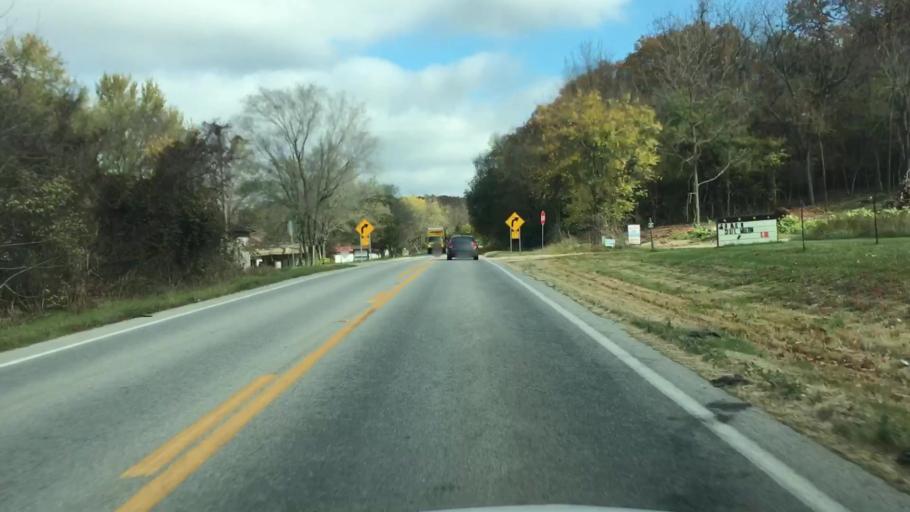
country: US
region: Arkansas
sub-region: Benton County
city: Gentry
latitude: 36.2593
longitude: -94.4247
